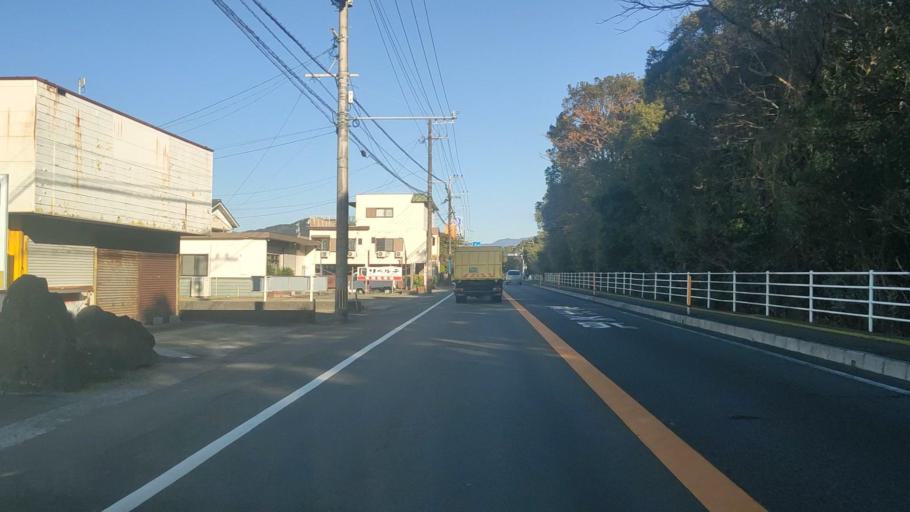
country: JP
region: Miyazaki
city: Nobeoka
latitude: 32.5271
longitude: 131.6822
